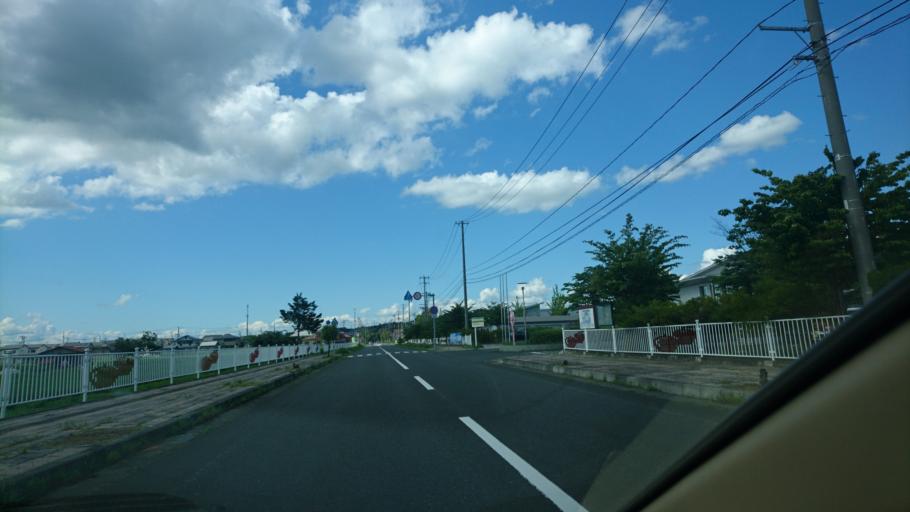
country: JP
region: Iwate
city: Mizusawa
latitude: 39.1798
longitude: 141.1809
